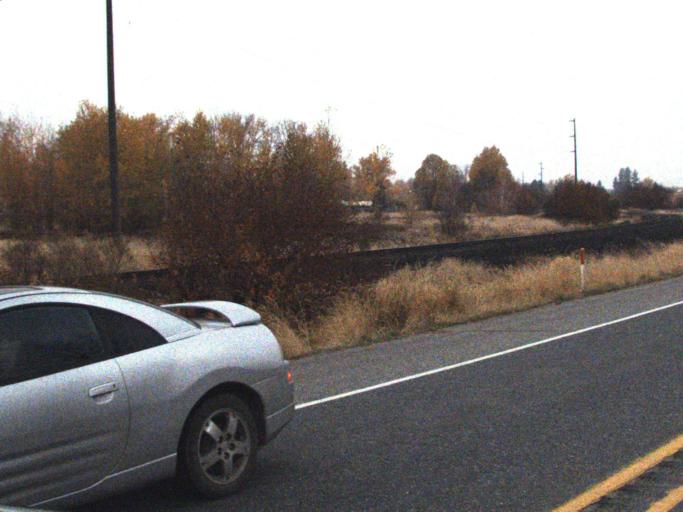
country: US
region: Washington
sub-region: Stevens County
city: Colville
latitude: 48.5826
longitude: -117.9612
